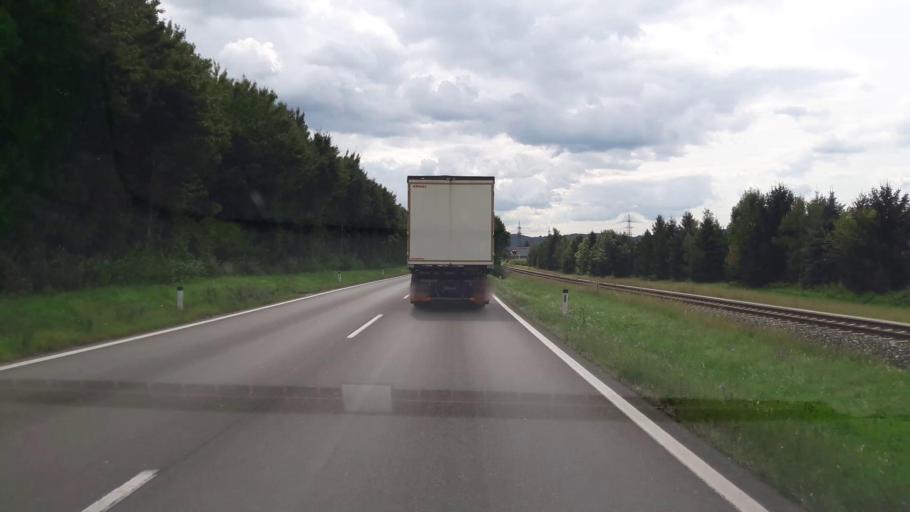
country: AT
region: Styria
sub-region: Politischer Bezirk Weiz
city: Gleisdorf
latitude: 47.1176
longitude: 15.7005
